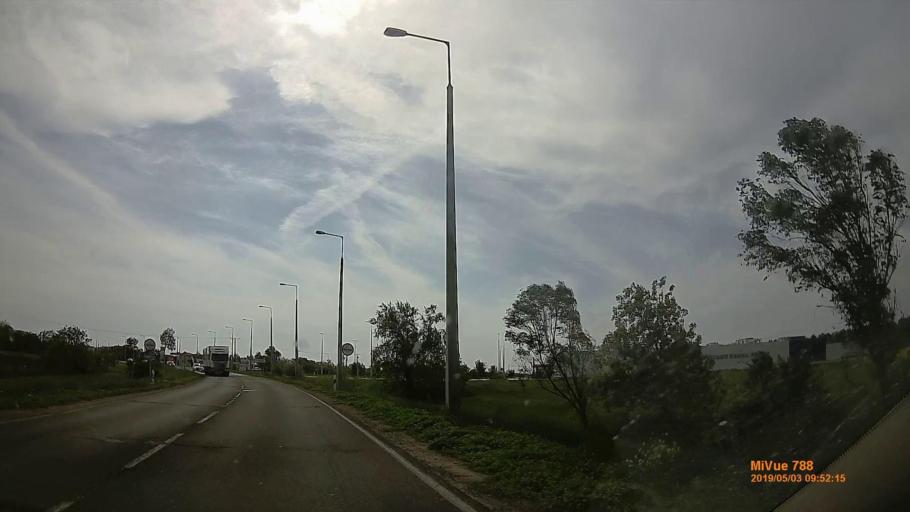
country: HU
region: Jasz-Nagykun-Szolnok
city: Torokszentmiklos
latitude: 47.1743
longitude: 20.3759
